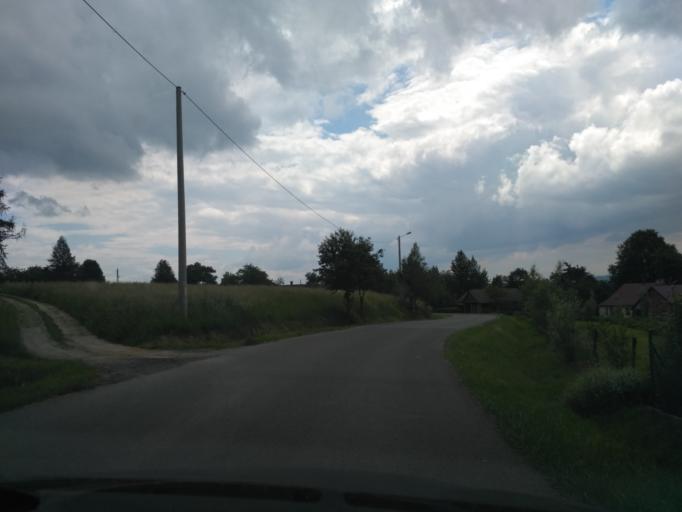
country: PL
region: Subcarpathian Voivodeship
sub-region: Powiat rzeszowski
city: Hyzne
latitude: 49.9371
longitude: 22.1784
